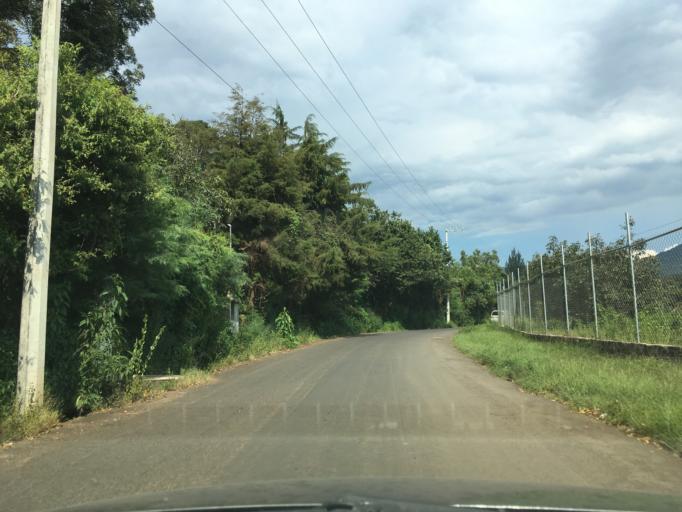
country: MX
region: Michoacan
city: Tingambato
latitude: 19.4998
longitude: -101.8638
